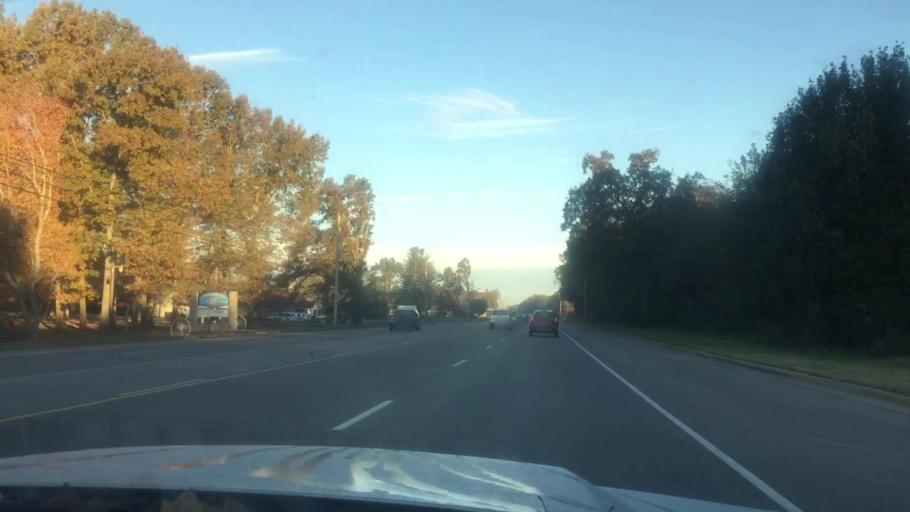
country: US
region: Tennessee
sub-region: Franklin County
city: Estill Springs
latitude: 35.2883
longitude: -86.1437
